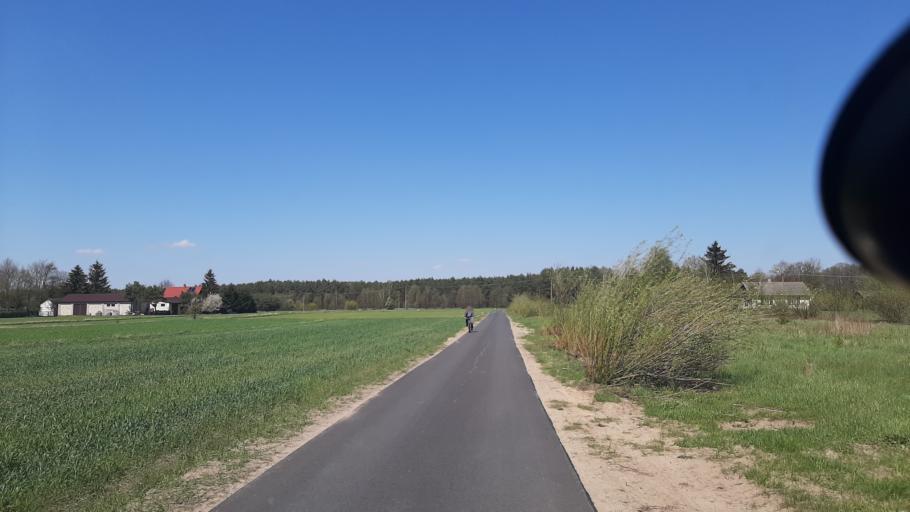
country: PL
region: Lublin Voivodeship
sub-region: Powiat lubelski
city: Garbow
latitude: 51.4040
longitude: 22.3224
